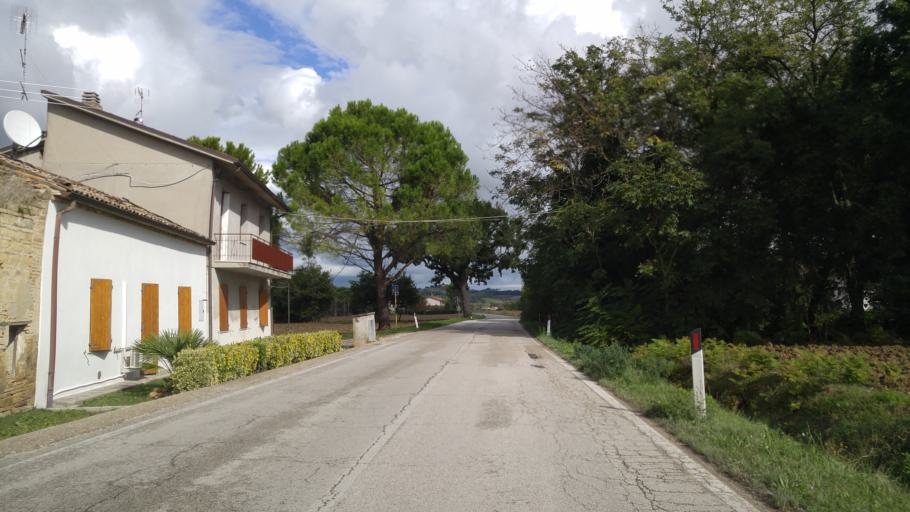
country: IT
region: The Marches
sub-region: Provincia di Pesaro e Urbino
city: Mombaroccio
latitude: 43.8352
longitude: 12.8794
